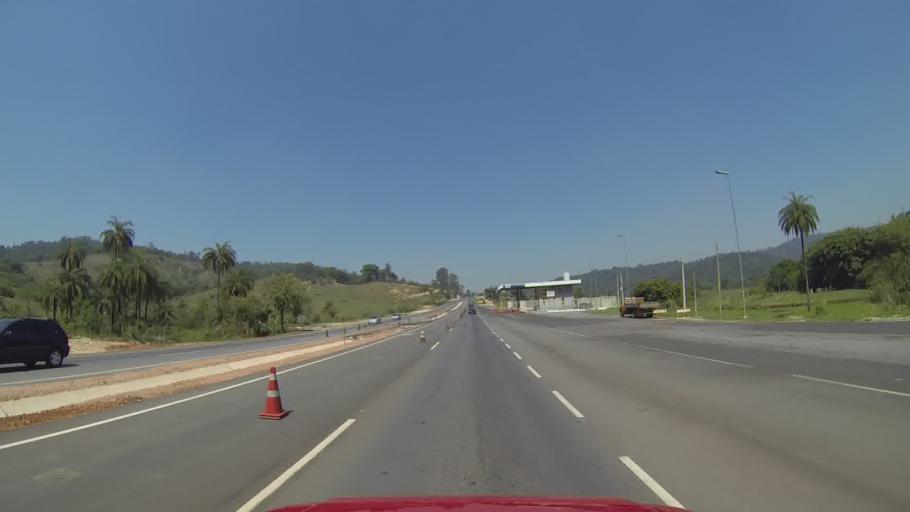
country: BR
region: Minas Gerais
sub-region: Mateus Leme
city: Mateus Leme
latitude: -20.0178
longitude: -44.4932
